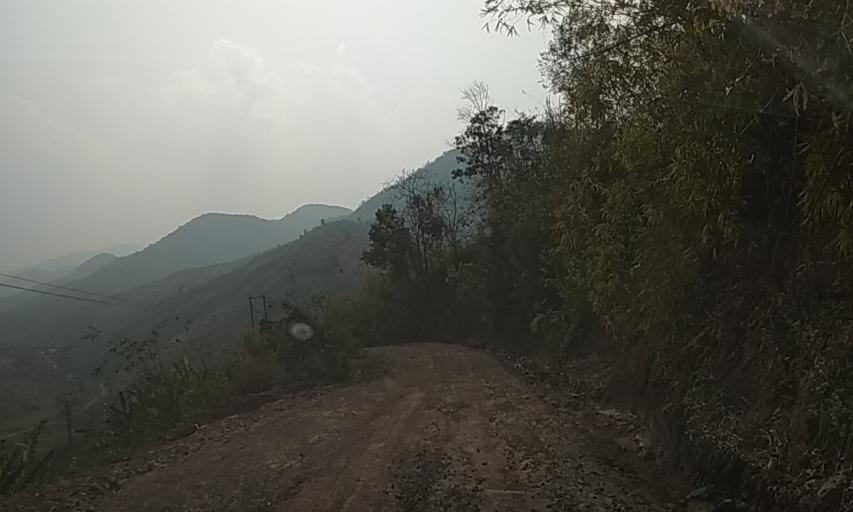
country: LA
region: Louangphabang
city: Louangphabang
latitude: 20.0394
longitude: 101.7991
